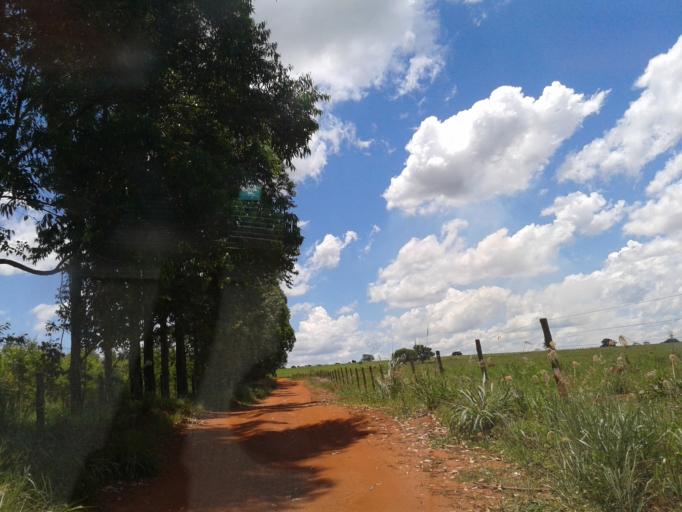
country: BR
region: Minas Gerais
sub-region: Centralina
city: Centralina
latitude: -18.7030
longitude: -49.1710
